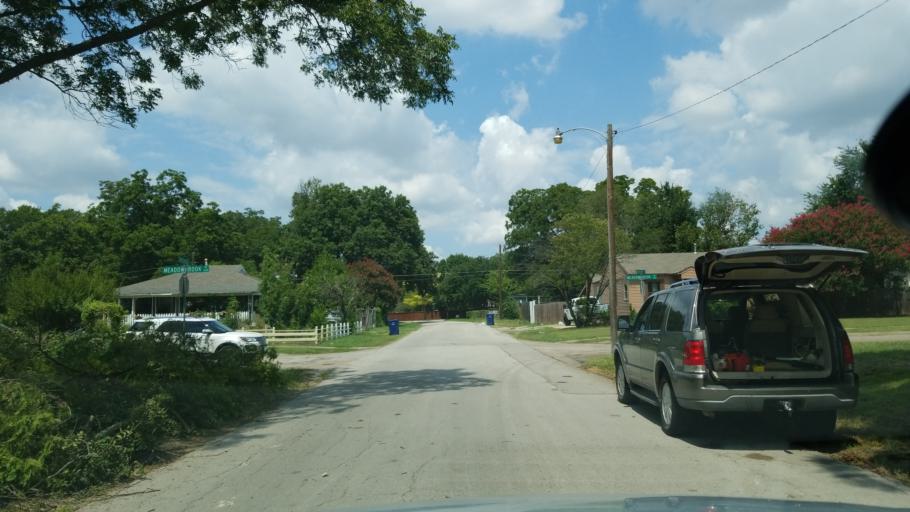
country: US
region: Texas
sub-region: Dallas County
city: Garland
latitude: 32.9196
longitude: -96.6553
